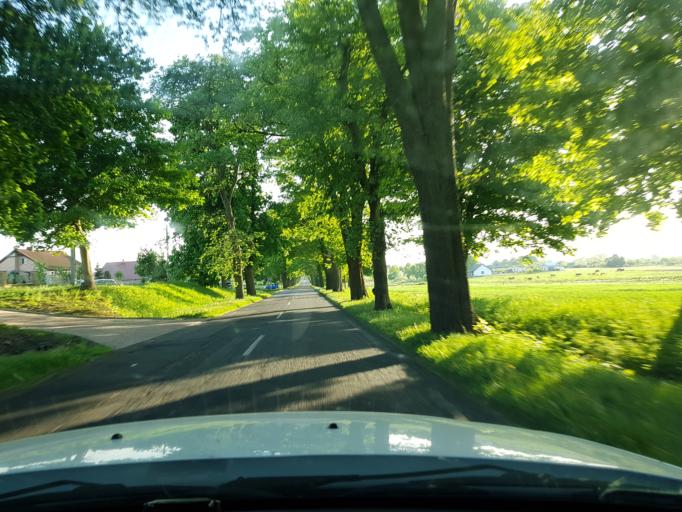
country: PL
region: West Pomeranian Voivodeship
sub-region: Powiat goleniowski
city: Maszewo
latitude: 53.5052
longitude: 15.0792
